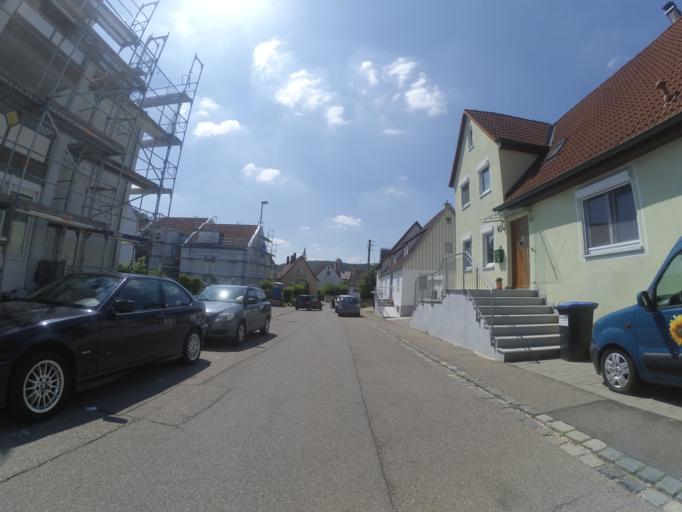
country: DE
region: Baden-Wuerttemberg
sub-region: Tuebingen Region
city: Dornstadt
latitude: 48.4242
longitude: 9.8953
